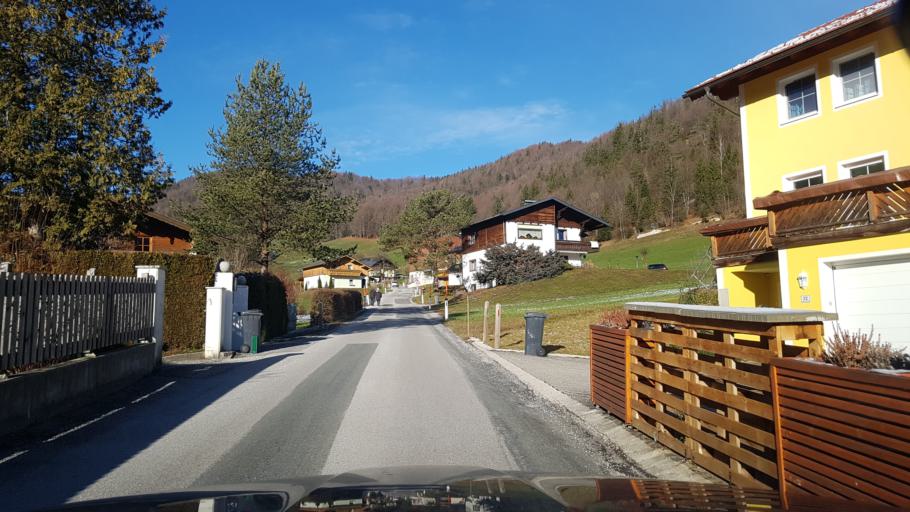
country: AT
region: Salzburg
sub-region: Politischer Bezirk Salzburg-Umgebung
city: Ebenau
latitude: 47.7713
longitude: 13.1728
